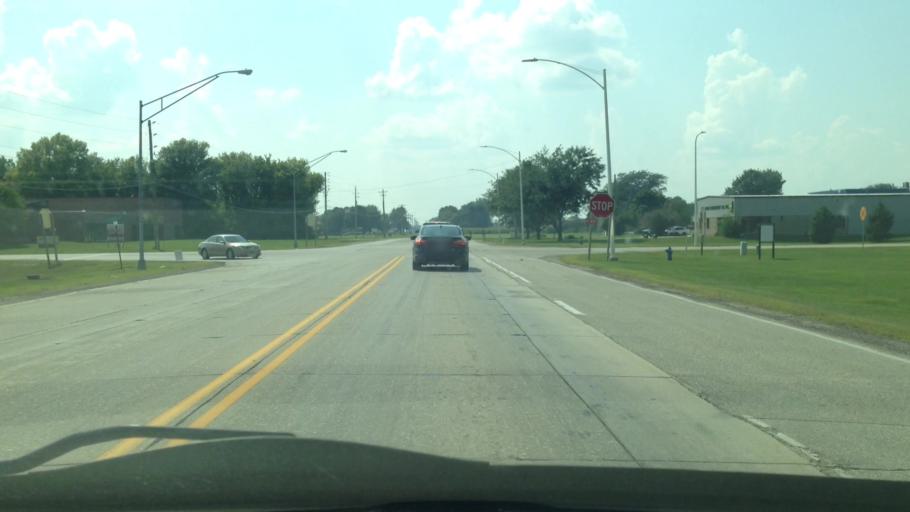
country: US
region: Iowa
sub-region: Black Hawk County
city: Cedar Falls
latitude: 42.5420
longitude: -92.3945
